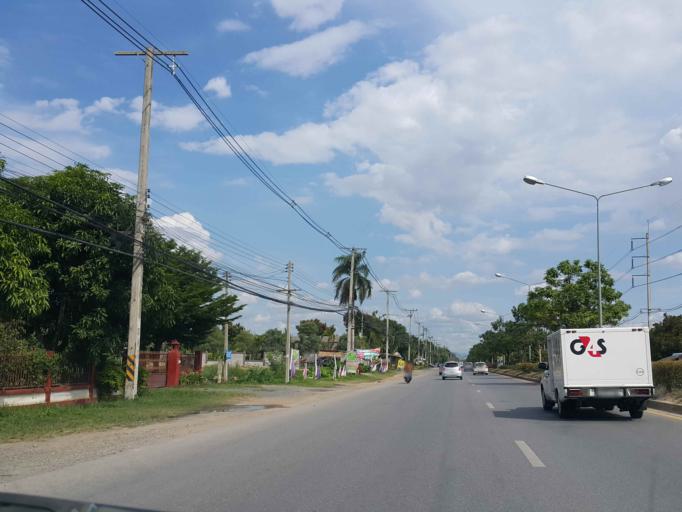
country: TH
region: Chiang Mai
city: San Sai
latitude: 18.9181
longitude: 98.9965
